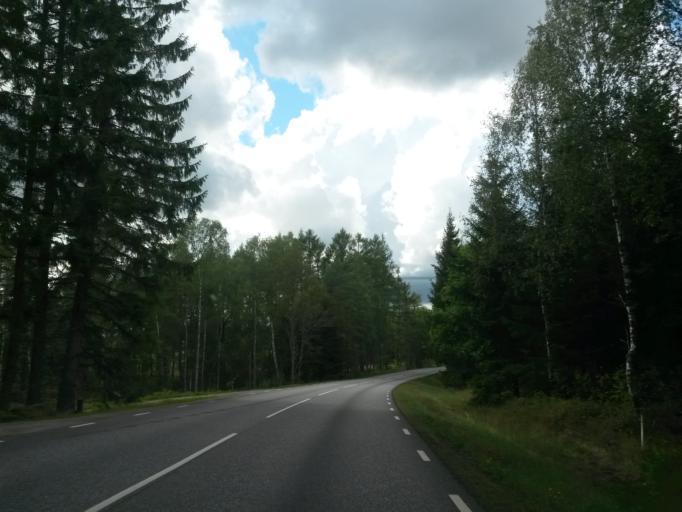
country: SE
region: Vaestra Goetaland
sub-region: Vargarda Kommun
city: Vargarda
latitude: 57.9899
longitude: 12.8263
